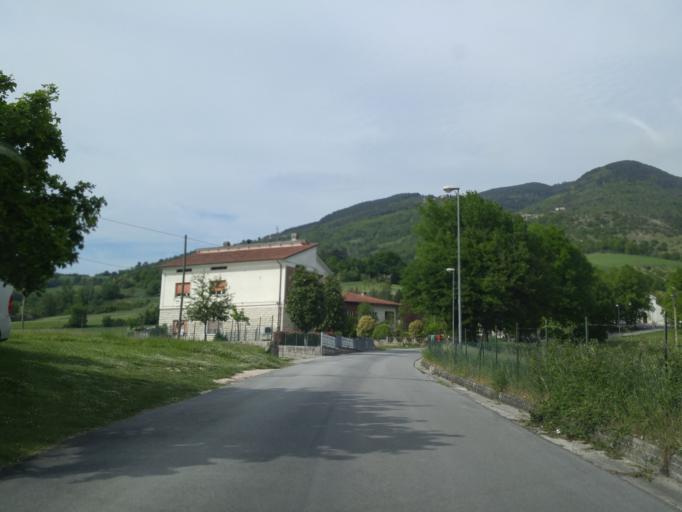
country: IT
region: The Marches
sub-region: Provincia di Pesaro e Urbino
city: Acqualagna
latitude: 43.6384
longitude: 12.6906
